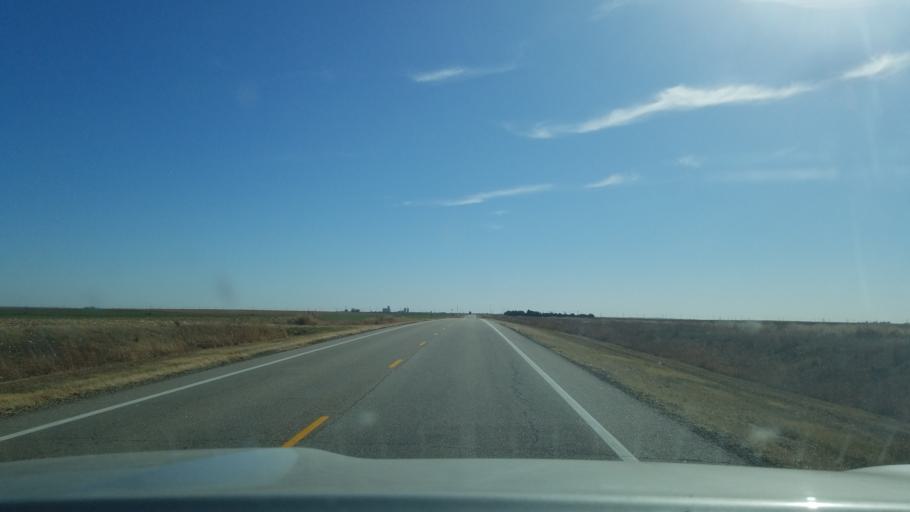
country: US
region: Kansas
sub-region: Kiowa County
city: Greensburg
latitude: 37.5794
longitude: -99.6743
